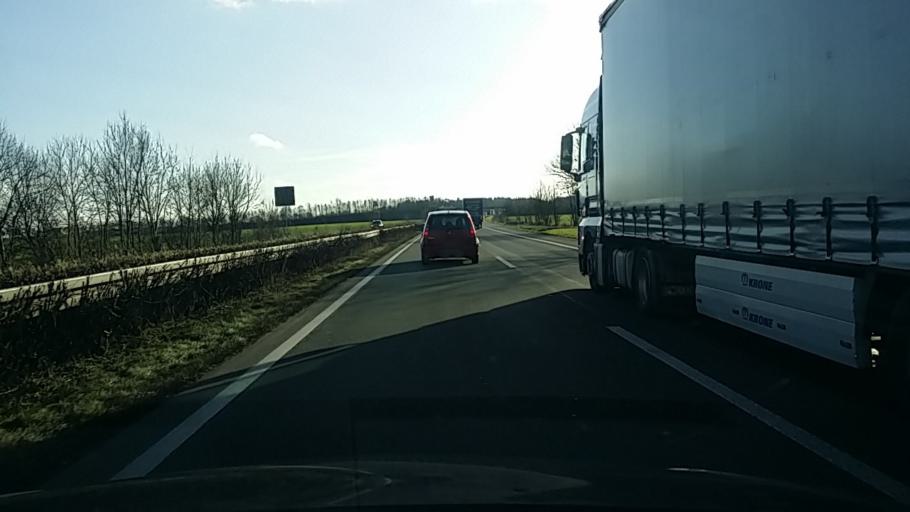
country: DE
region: North Rhine-Westphalia
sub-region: Regierungsbezirk Detmold
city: Paderborn
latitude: 51.6272
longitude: 8.7253
